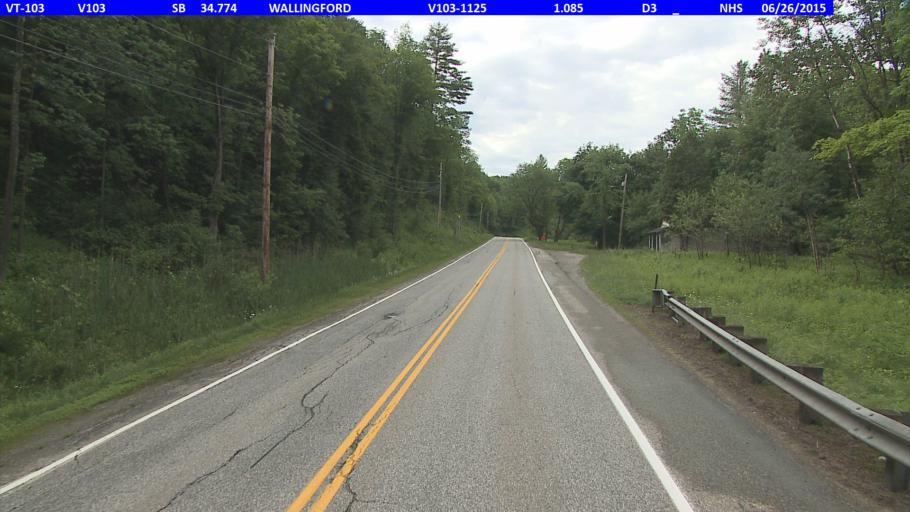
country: US
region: Vermont
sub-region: Rutland County
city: Rutland
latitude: 43.4655
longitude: -72.8747
